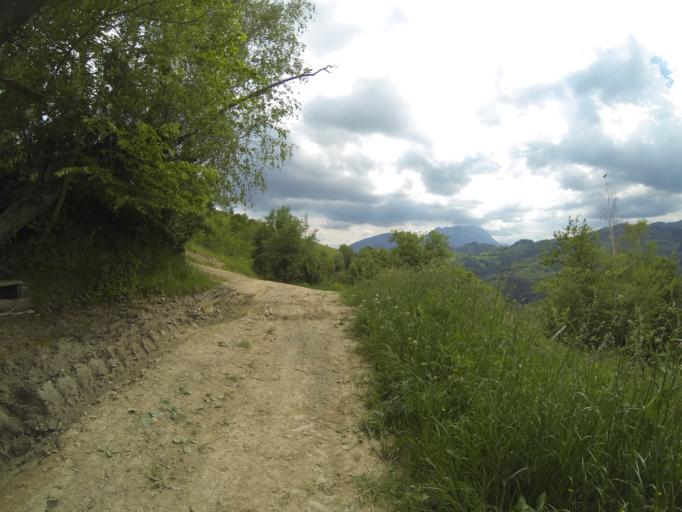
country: RO
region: Brasov
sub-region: Comuna Poiana Marului
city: Poiana Marului
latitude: 45.6396
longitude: 25.2900
